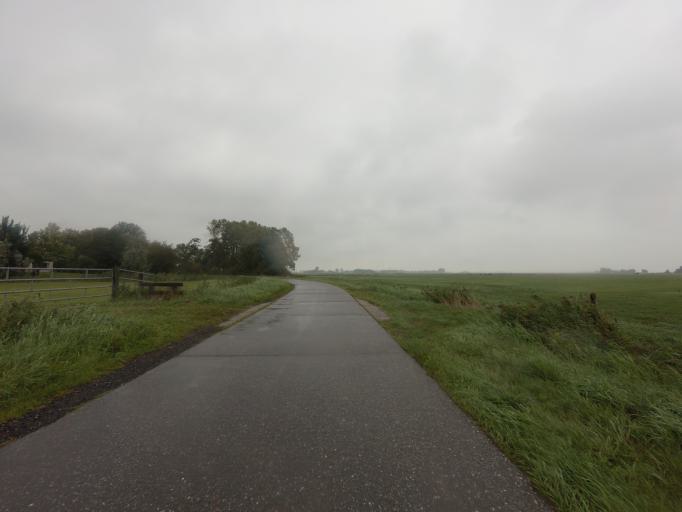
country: NL
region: Friesland
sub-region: Gemeente Boarnsterhim
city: Nes
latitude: 53.0331
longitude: 5.8689
